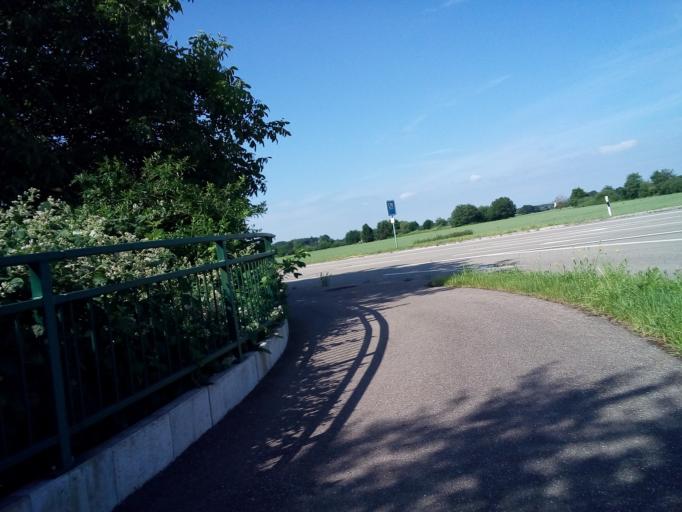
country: DE
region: Baden-Wuerttemberg
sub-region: Freiburg Region
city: Rheinau
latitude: 48.6326
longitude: 7.9210
